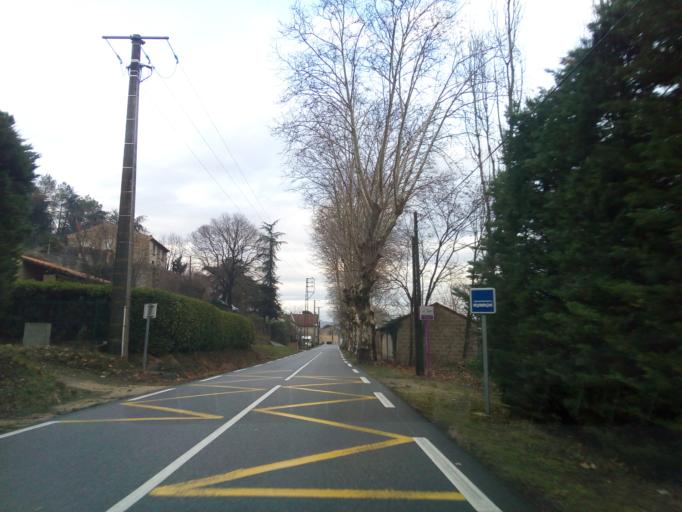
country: FR
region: Rhone-Alpes
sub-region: Departement de l'Ardeche
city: Saint-Laurent-du-Pape
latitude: 44.8238
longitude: 4.7446
